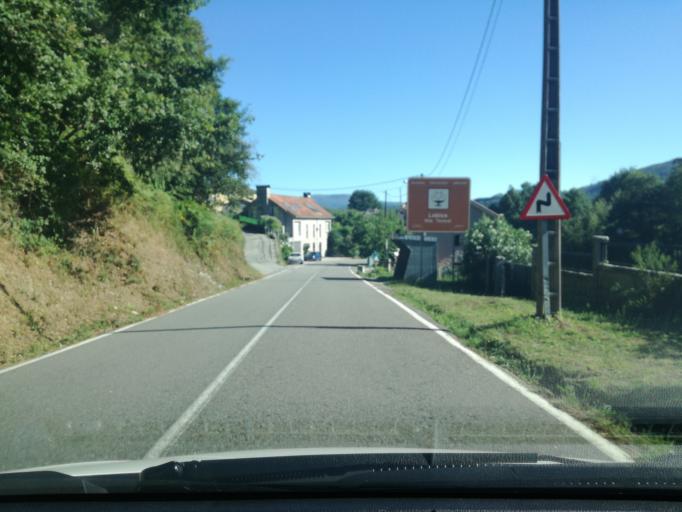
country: ES
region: Galicia
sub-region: Provincia de Ourense
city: Lobios
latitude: 41.8639
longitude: -8.1073
